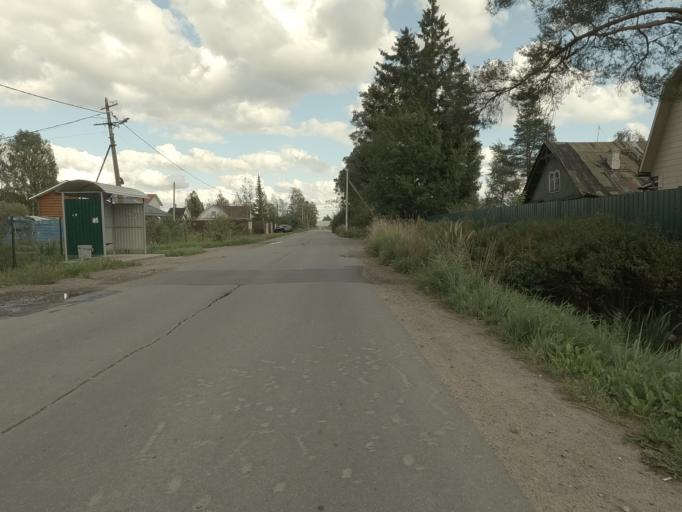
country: RU
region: Leningrad
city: Ul'yanovka
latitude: 59.6330
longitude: 30.7798
